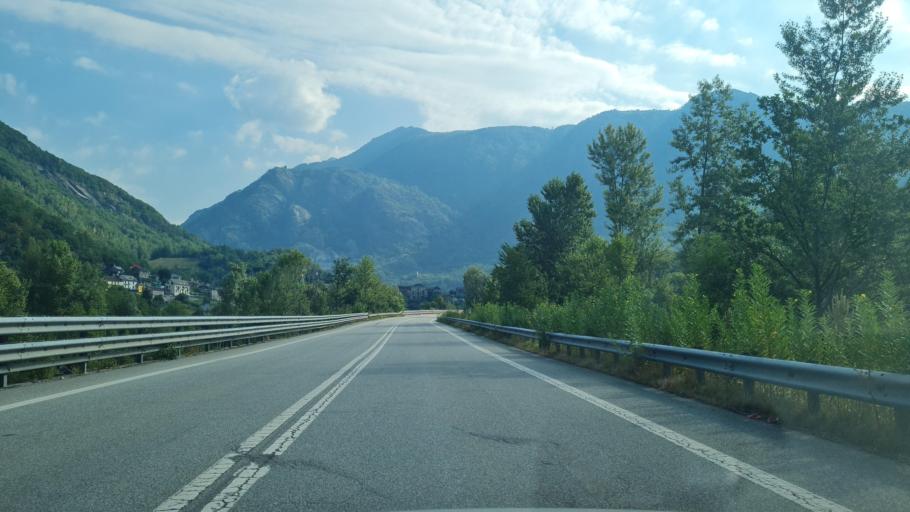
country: IT
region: Piedmont
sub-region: Provincia Verbano-Cusio-Ossola
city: Montecrestese
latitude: 46.1695
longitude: 8.3130
